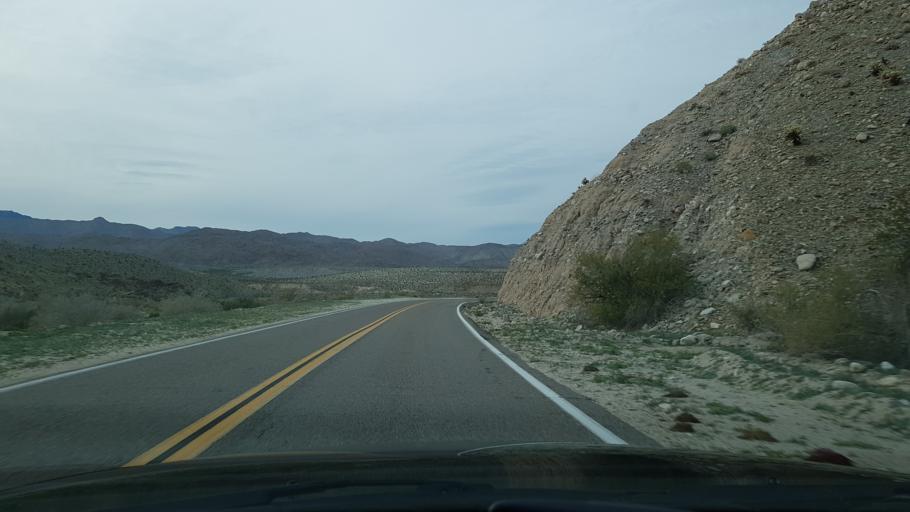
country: US
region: California
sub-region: San Diego County
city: Pine Valley
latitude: 32.8385
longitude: -116.1935
